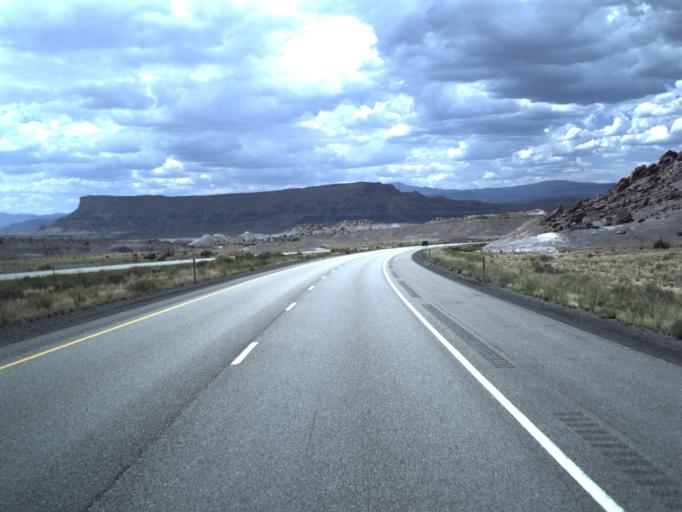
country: US
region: Utah
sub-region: Emery County
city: Ferron
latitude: 38.8201
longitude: -111.1543
